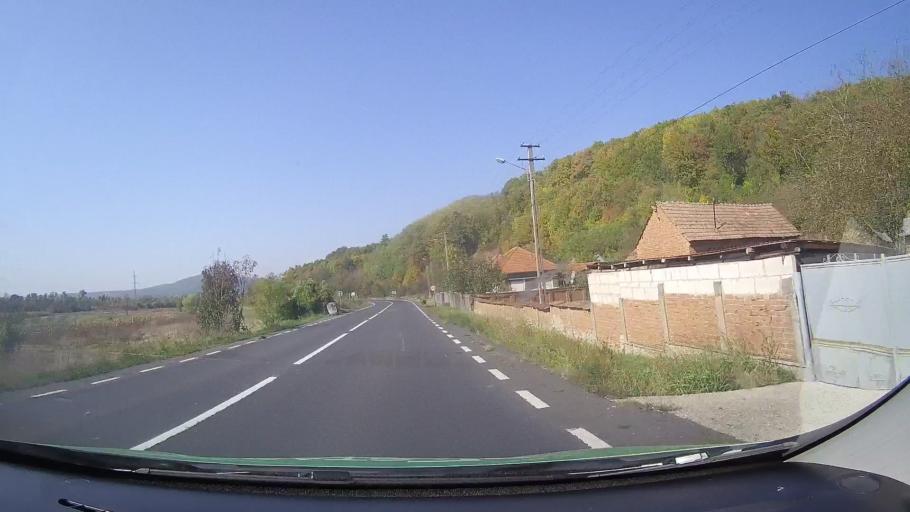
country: RO
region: Hunedoara
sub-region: Comuna Dobra
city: Dobra
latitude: 45.9397
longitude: 22.5360
